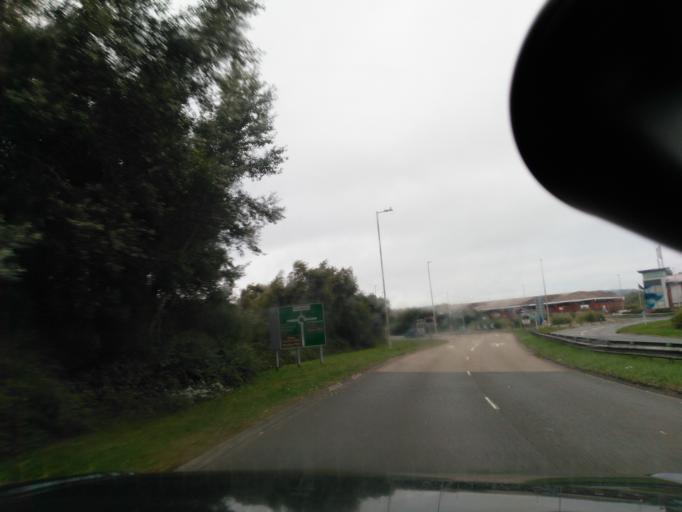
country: GB
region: England
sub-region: Poole
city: Poole
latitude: 50.7351
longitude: -1.9939
